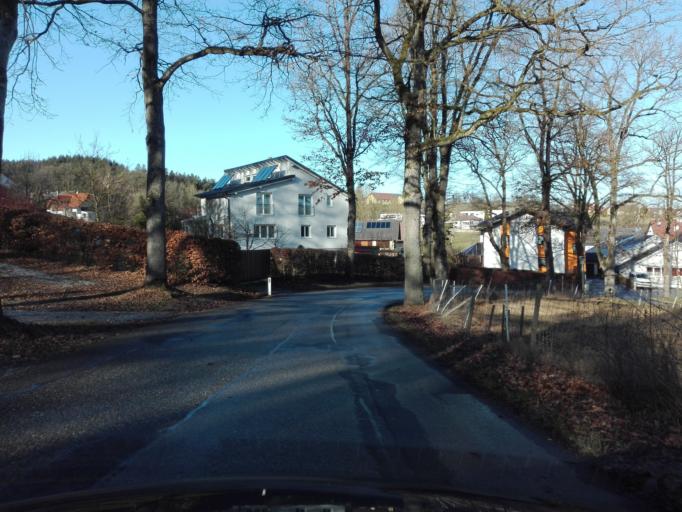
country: AT
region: Upper Austria
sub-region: Politischer Bezirk Perg
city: Bad Kreuzen
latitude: 48.2228
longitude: 14.7812
